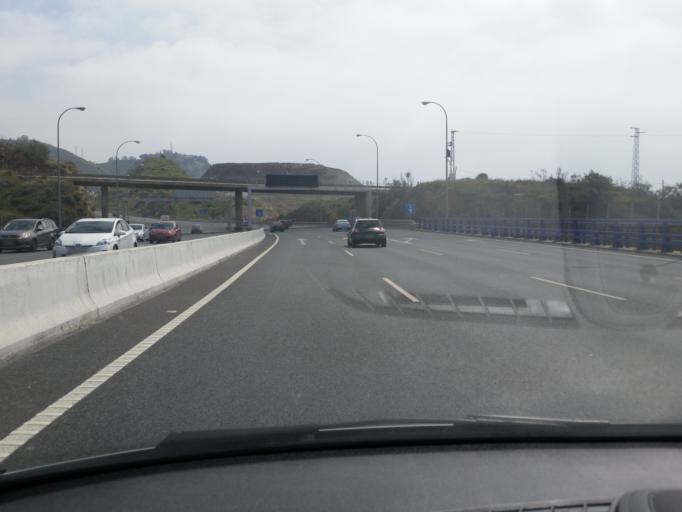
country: ES
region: Andalusia
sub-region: Provincia de Malaga
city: Malaga
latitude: 36.7409
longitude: -4.4016
